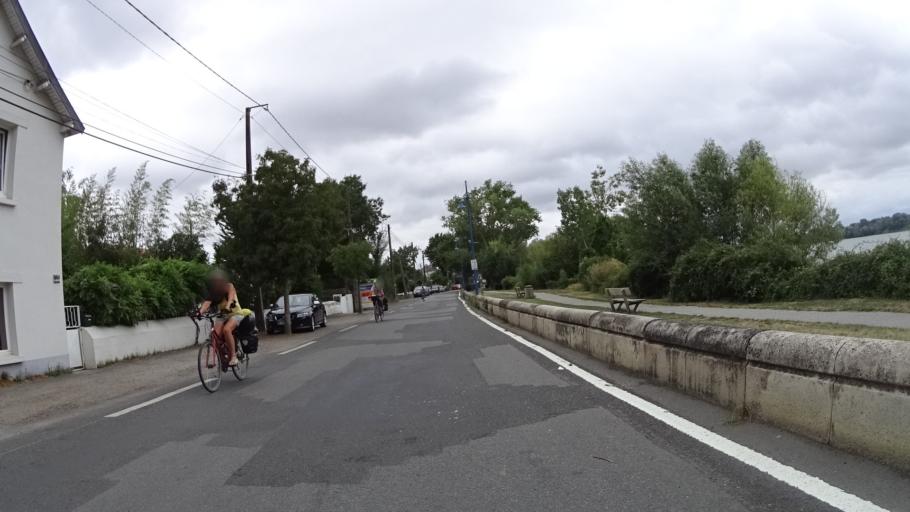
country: FR
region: Pays de la Loire
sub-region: Departement de la Loire-Atlantique
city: Sainte-Luce-sur-Loire
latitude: 47.2349
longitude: -1.4739
